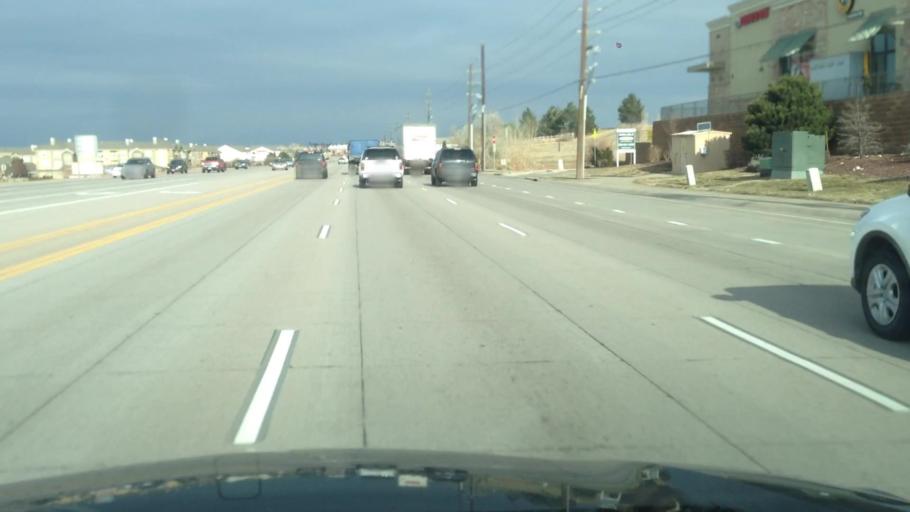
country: US
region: Colorado
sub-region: Arapahoe County
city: Dove Valley
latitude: 39.6033
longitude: -104.8067
